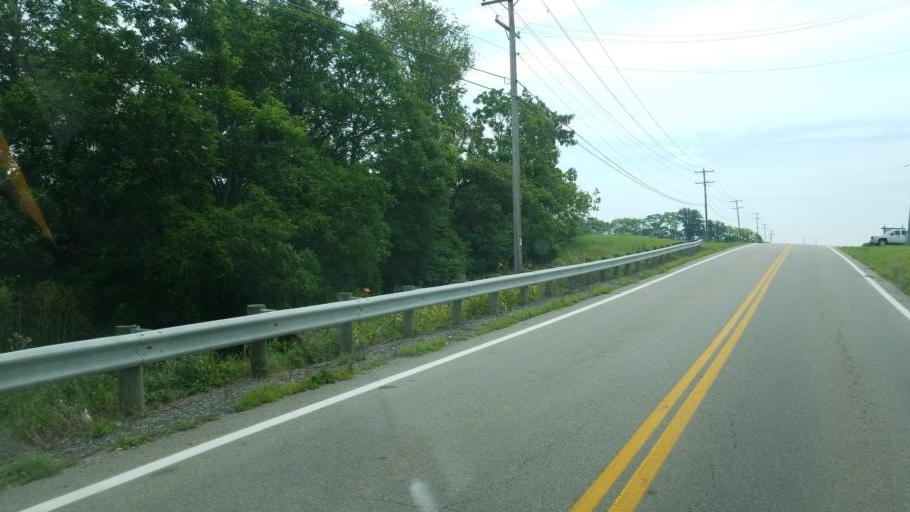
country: US
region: Ohio
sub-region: Madison County
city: West Jefferson
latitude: 39.9731
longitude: -83.3744
